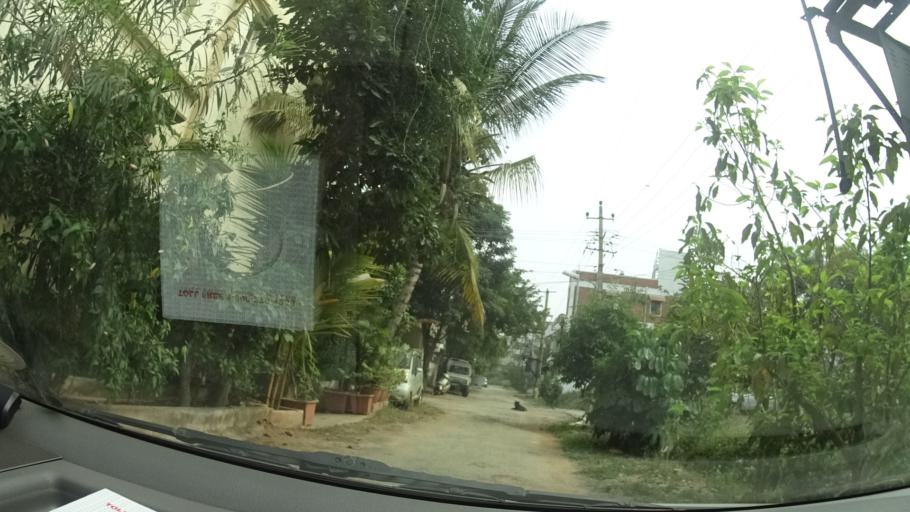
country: IN
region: Karnataka
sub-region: Bangalore Urban
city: Yelahanka
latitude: 13.0437
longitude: 77.6221
